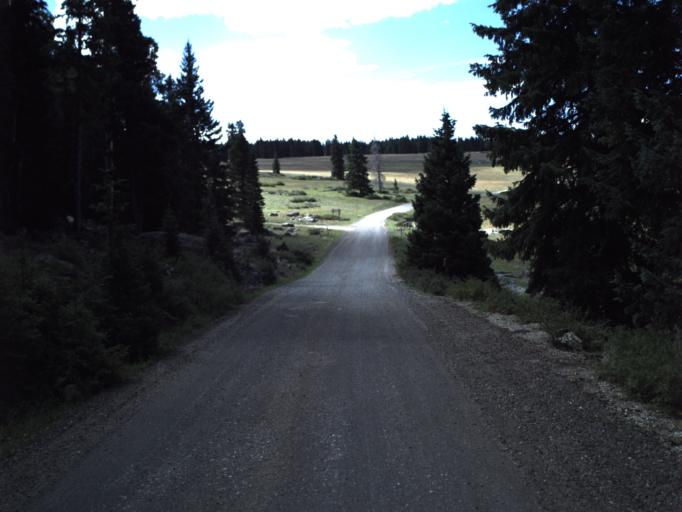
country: US
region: Utah
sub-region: Piute County
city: Junction
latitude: 38.2868
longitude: -112.3577
